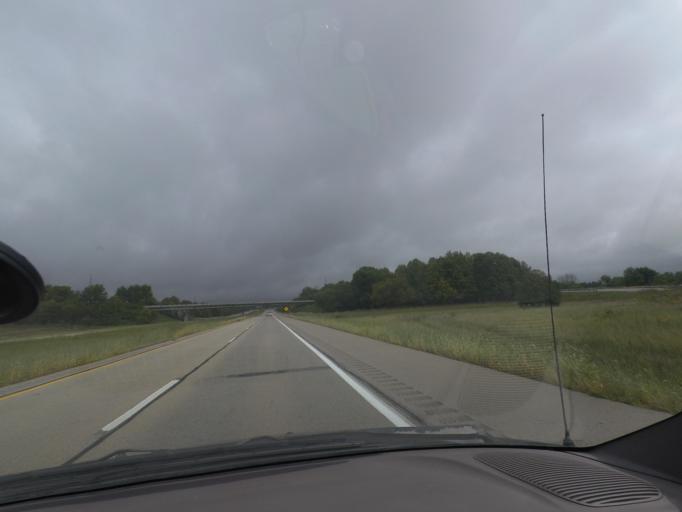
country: US
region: Illinois
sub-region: Piatt County
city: Monticello
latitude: 40.0817
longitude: -88.5273
